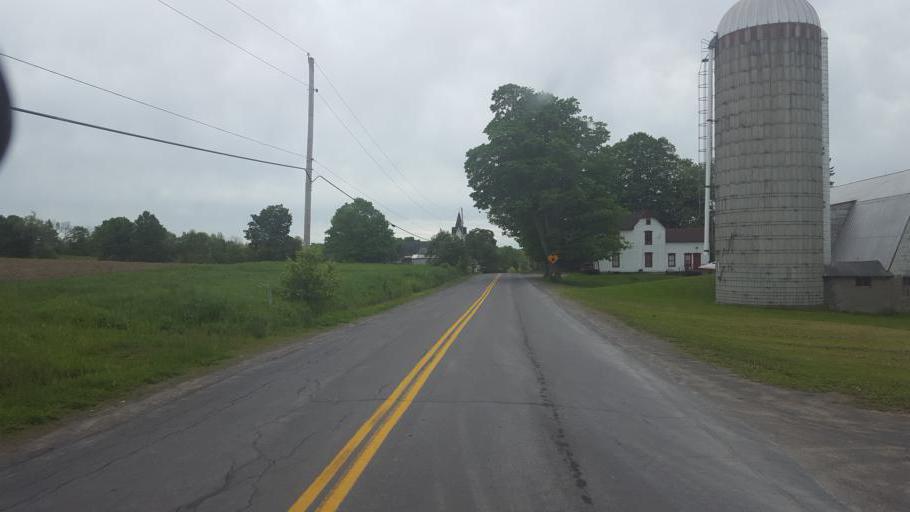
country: US
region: New York
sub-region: Herkimer County
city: Ilion
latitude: 42.9347
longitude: -75.0353
